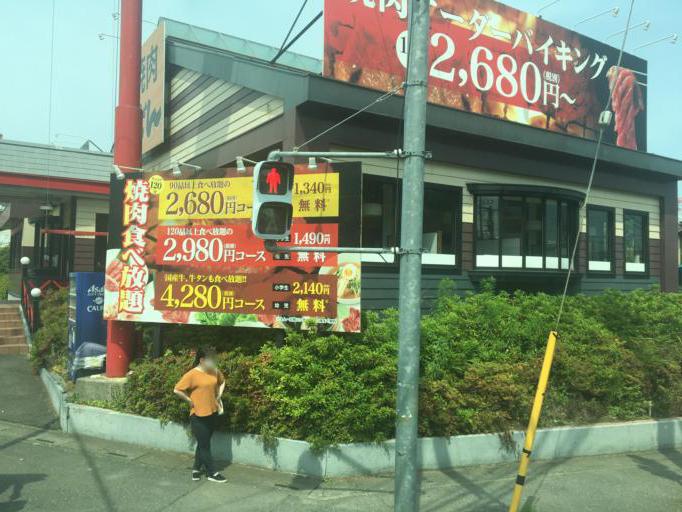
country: JP
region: Saitama
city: Asaka
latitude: 35.7707
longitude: 139.5650
